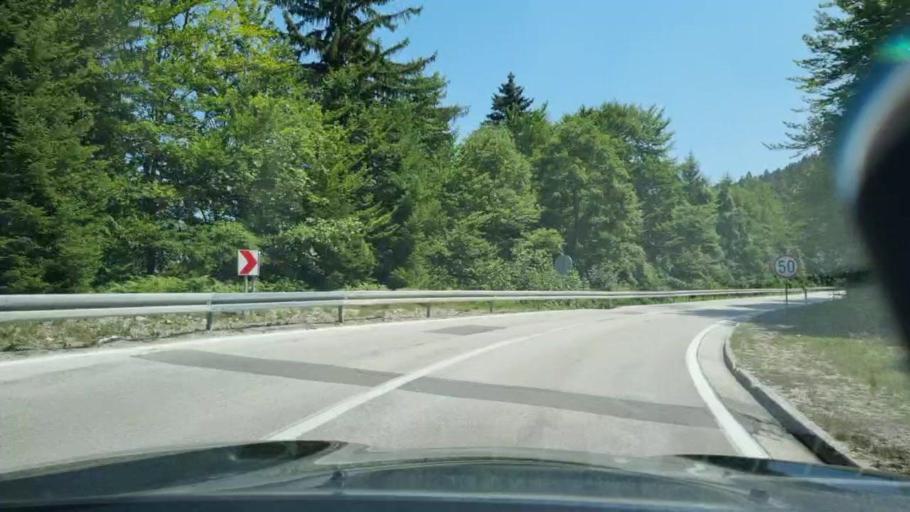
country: BA
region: Federation of Bosnia and Herzegovina
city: Sanica
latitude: 44.5059
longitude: 16.3587
